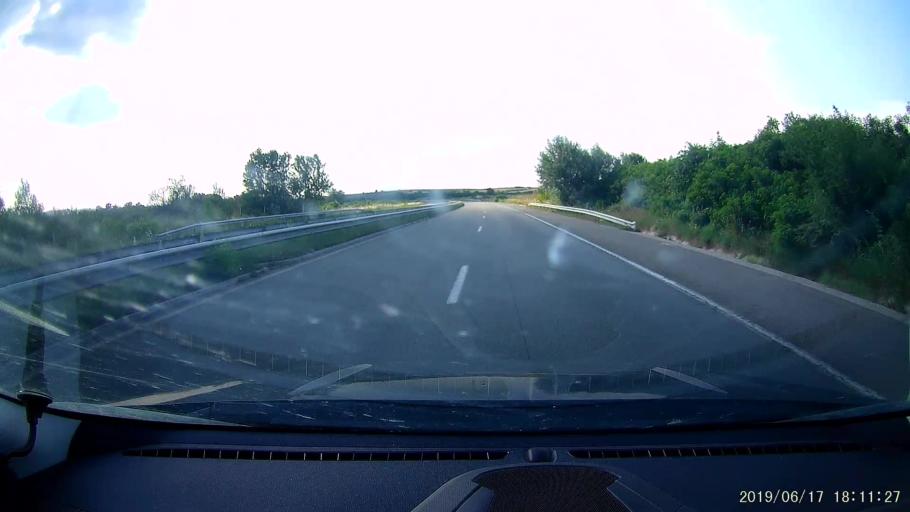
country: BG
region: Khaskovo
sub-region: Obshtina Lyubimets
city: Lyubimets
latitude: 41.8845
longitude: 26.0510
